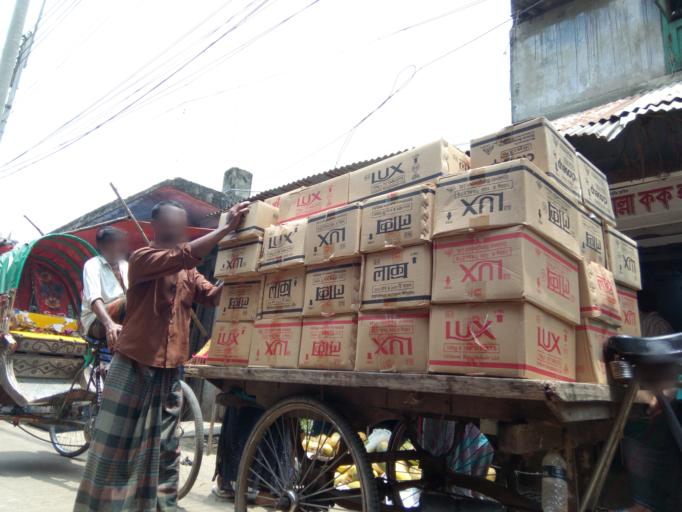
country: BD
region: Dhaka
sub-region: Dhaka
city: Dhaka
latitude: 23.7159
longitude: 90.3989
